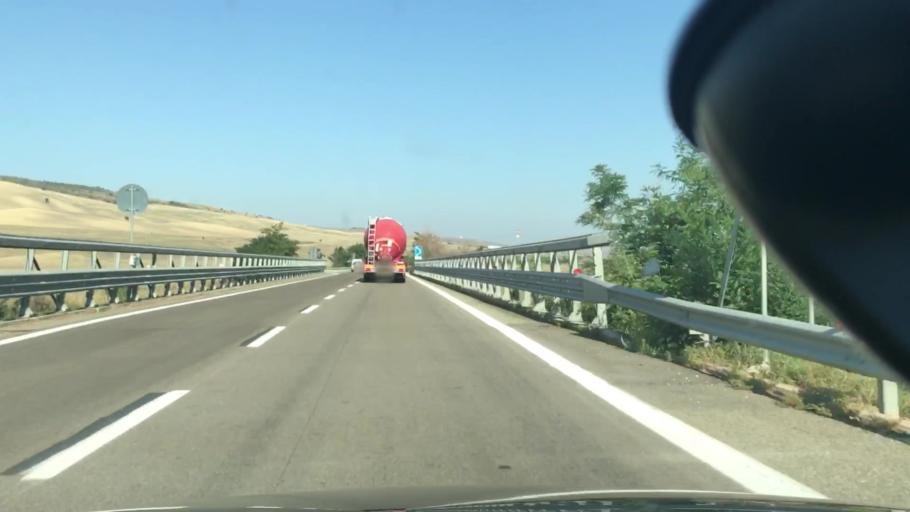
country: IT
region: Basilicate
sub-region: Provincia di Matera
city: Irsina
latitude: 40.7914
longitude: 16.2828
